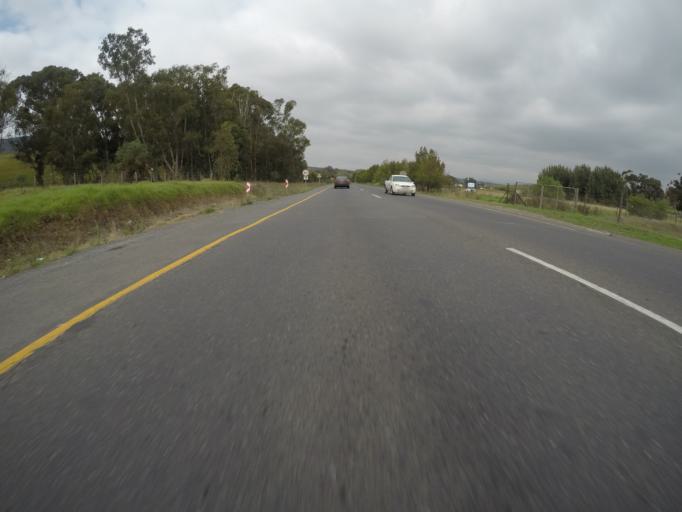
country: ZA
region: Western Cape
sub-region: City of Cape Town
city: Sunset Beach
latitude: -33.8387
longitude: 18.5959
